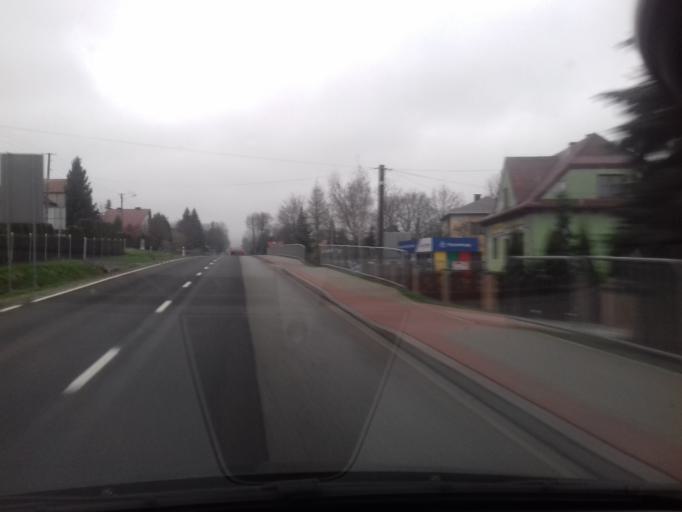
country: PL
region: Lesser Poland Voivodeship
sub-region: Powiat limanowski
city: Dobra
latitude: 49.7155
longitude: 20.2558
